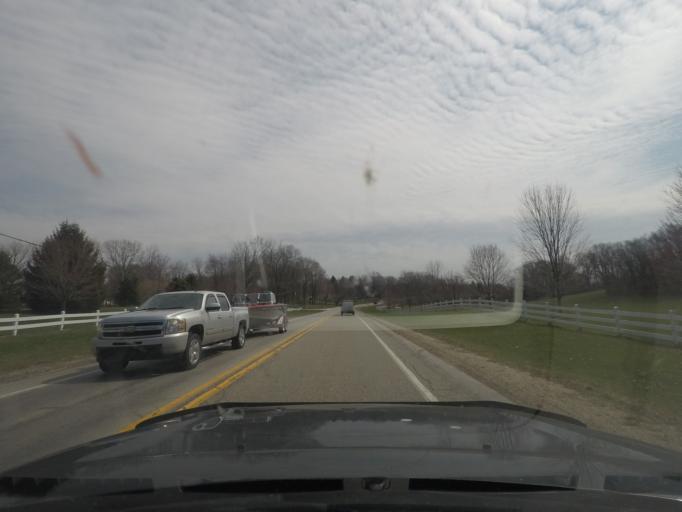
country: US
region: Indiana
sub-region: LaPorte County
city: LaPorte
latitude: 41.6451
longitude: -86.7500
